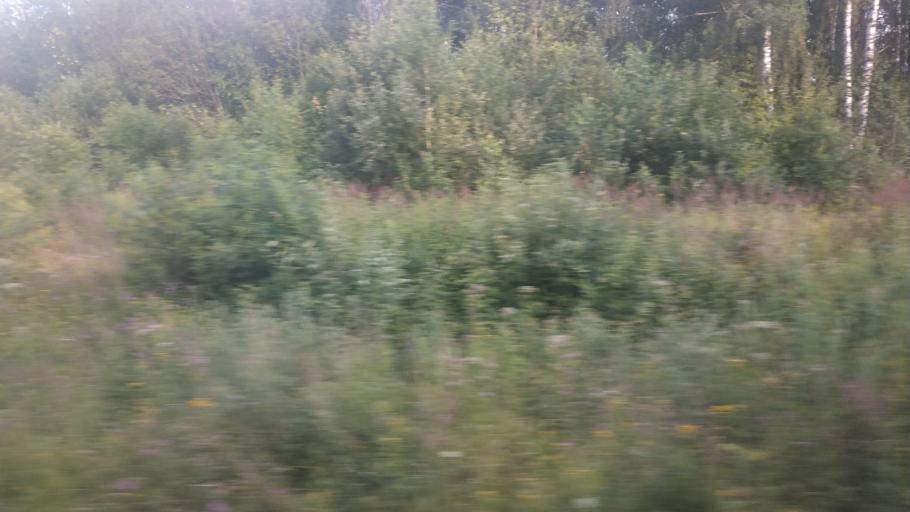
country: RU
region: Moskovskaya
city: Tugolesskiy Bor
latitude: 55.5524
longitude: 39.6950
